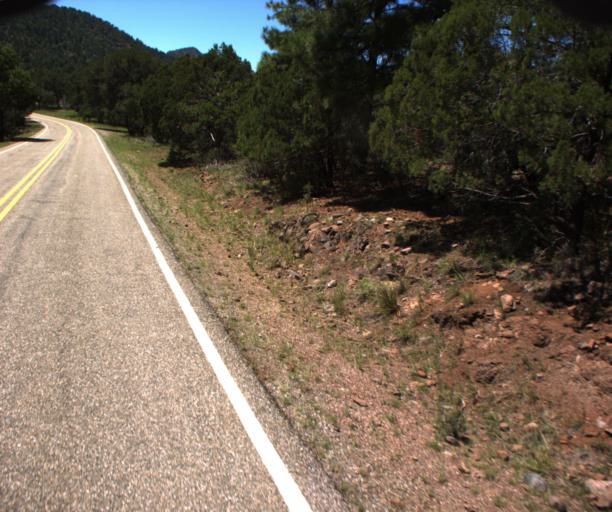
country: US
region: Arizona
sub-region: Greenlee County
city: Morenci
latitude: 33.2450
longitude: -109.3745
